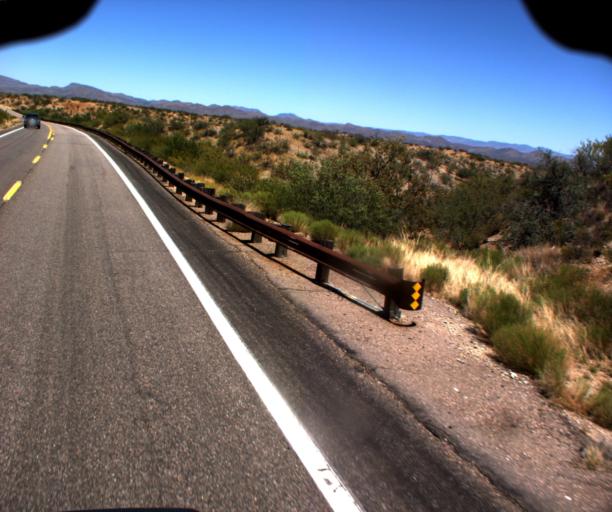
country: US
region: Arizona
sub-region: Gila County
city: Globe
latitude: 33.3352
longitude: -110.7285
